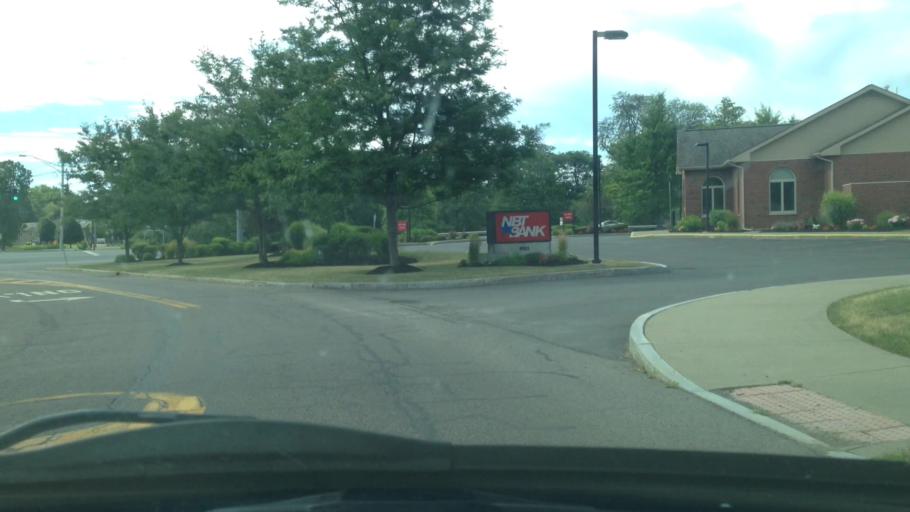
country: US
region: New York
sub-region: Onondaga County
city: East Syracuse
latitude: 43.0883
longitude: -76.0801
